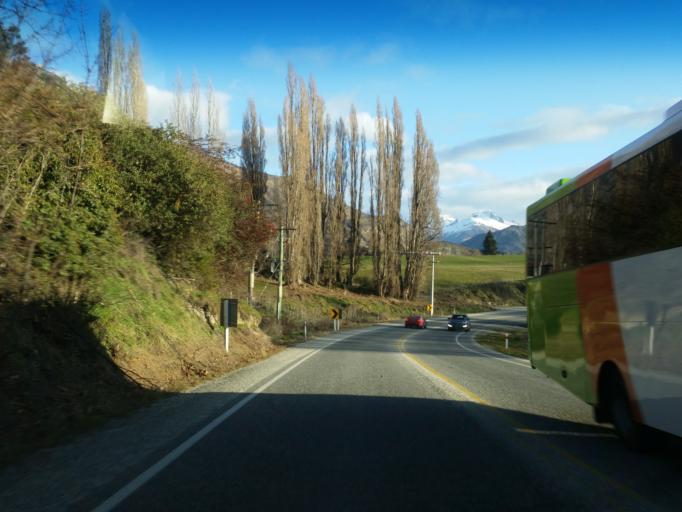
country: NZ
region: Otago
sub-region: Queenstown-Lakes District
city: Arrowtown
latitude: -44.9946
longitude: 168.8050
